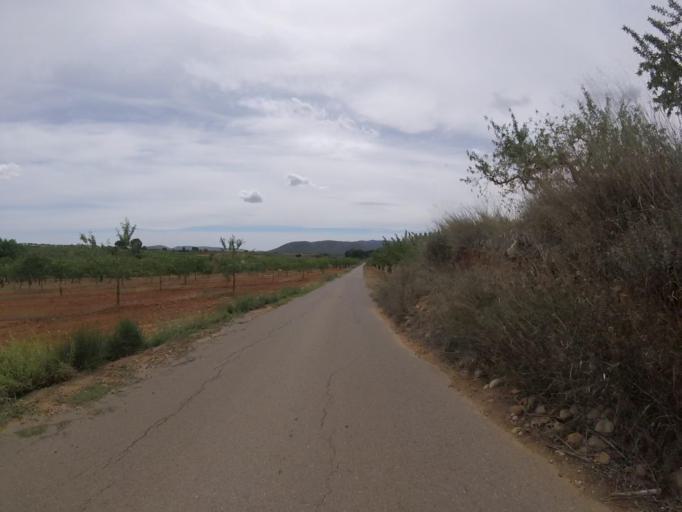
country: ES
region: Valencia
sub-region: Provincia de Castello
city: Benlloch
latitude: 40.1814
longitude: -0.0073
